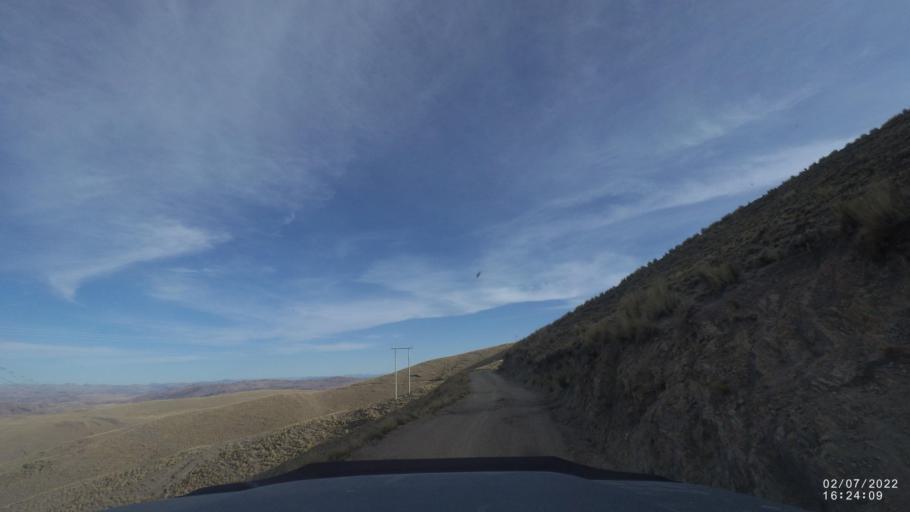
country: BO
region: Cochabamba
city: Irpa Irpa
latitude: -17.9397
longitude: -66.4615
